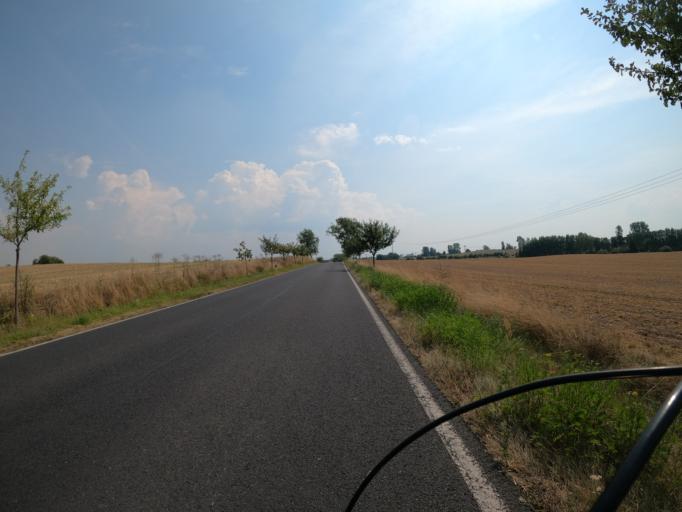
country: DE
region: Brandenburg
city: Angermunde
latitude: 53.0397
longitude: 13.9707
